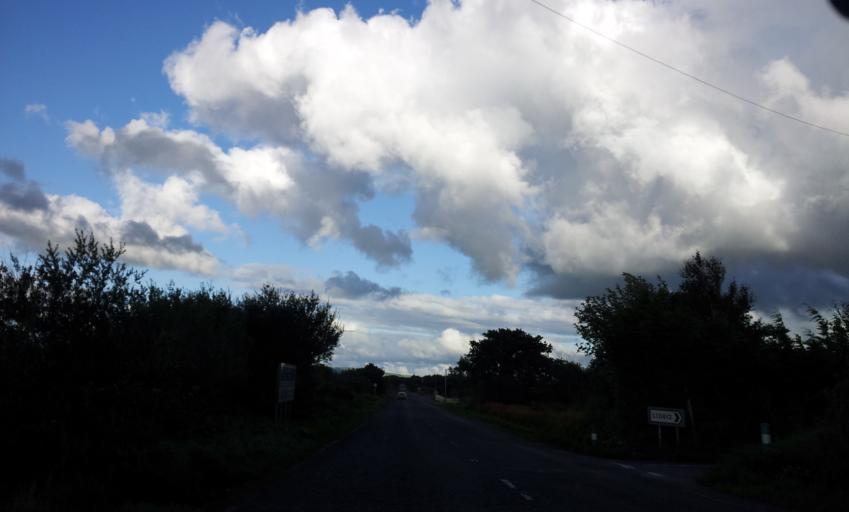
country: IE
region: Munster
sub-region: Ciarrai
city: Tralee
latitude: 52.2447
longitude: -9.7680
